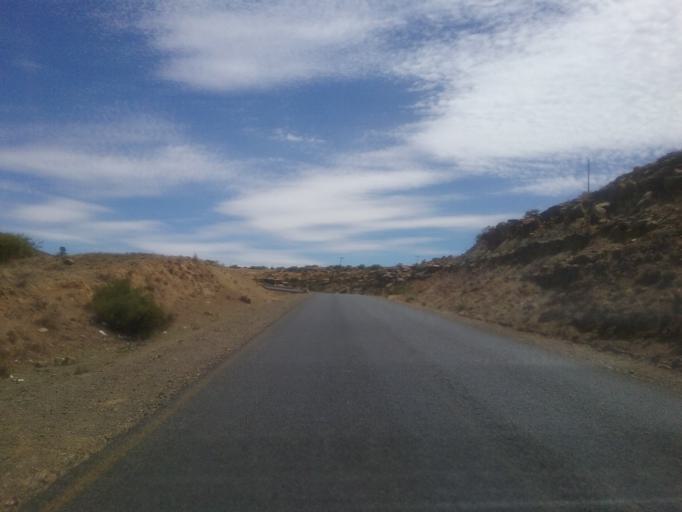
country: LS
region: Mohale's Hoek District
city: Mohale's Hoek
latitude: -30.0792
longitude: 27.4277
